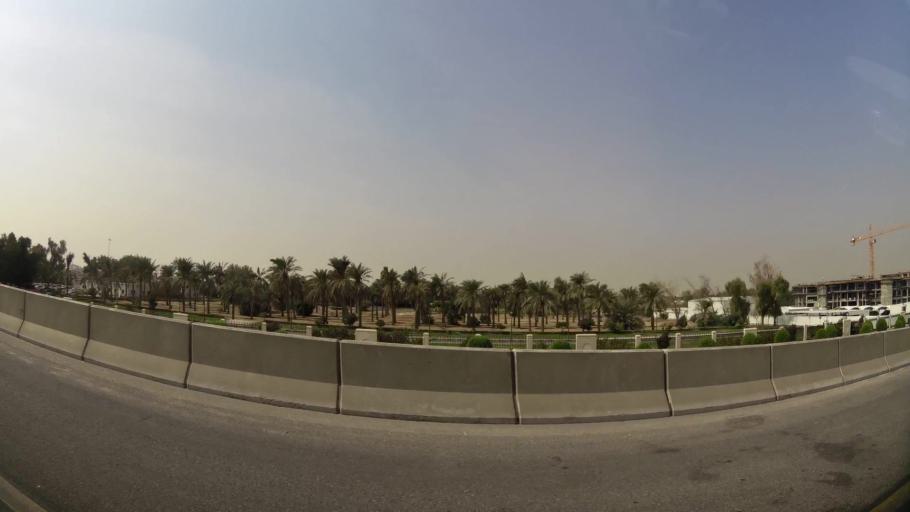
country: KW
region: Al Asimah
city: Ar Rabiyah
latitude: 29.2912
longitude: 47.9473
